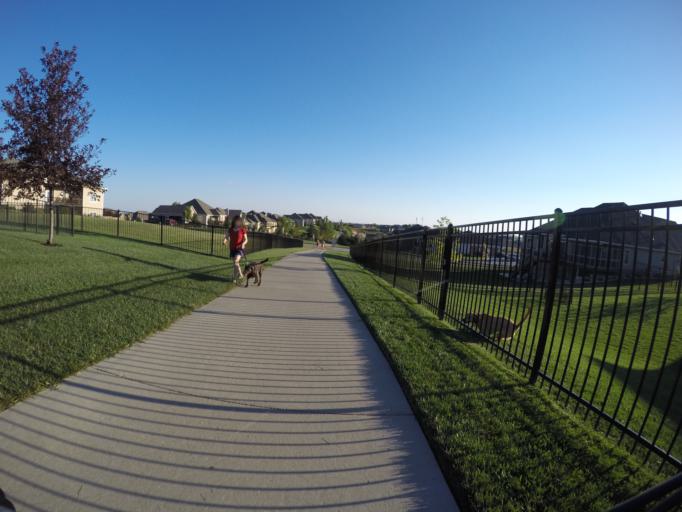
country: US
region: Kansas
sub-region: Riley County
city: Manhattan
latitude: 39.2176
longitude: -96.6261
